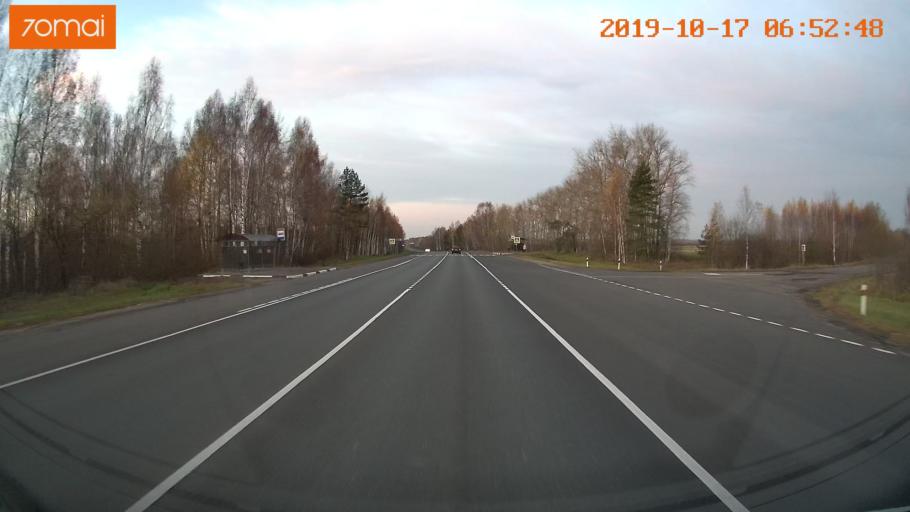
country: RU
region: Vladimir
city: Kideksha
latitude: 56.4822
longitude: 40.4995
